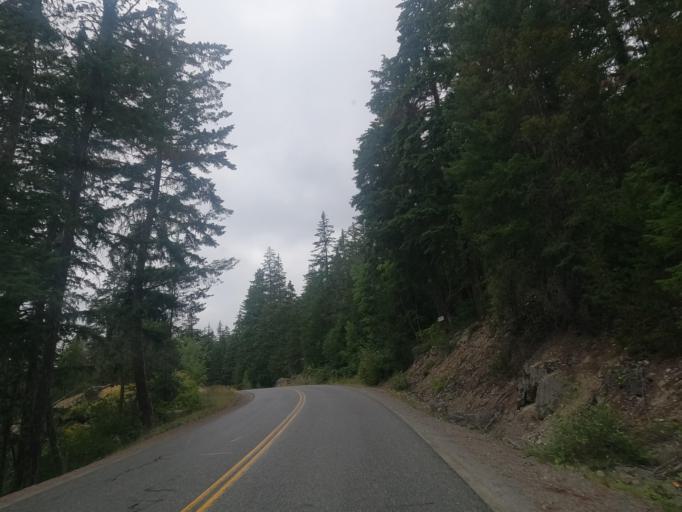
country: CA
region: British Columbia
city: Pemberton
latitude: 50.3050
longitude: -122.5764
